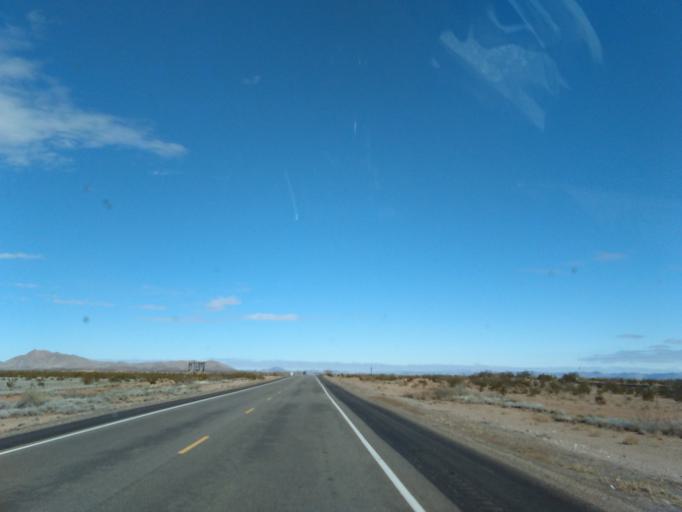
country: US
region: New Mexico
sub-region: Luna County
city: Deming
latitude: 32.3200
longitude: -107.6775
